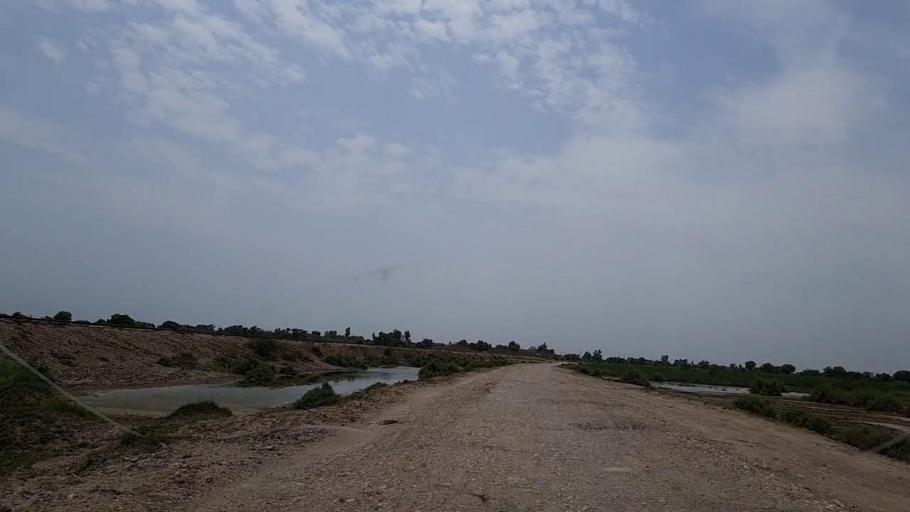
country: PK
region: Sindh
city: Tharu Shah
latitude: 26.9293
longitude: 68.0886
